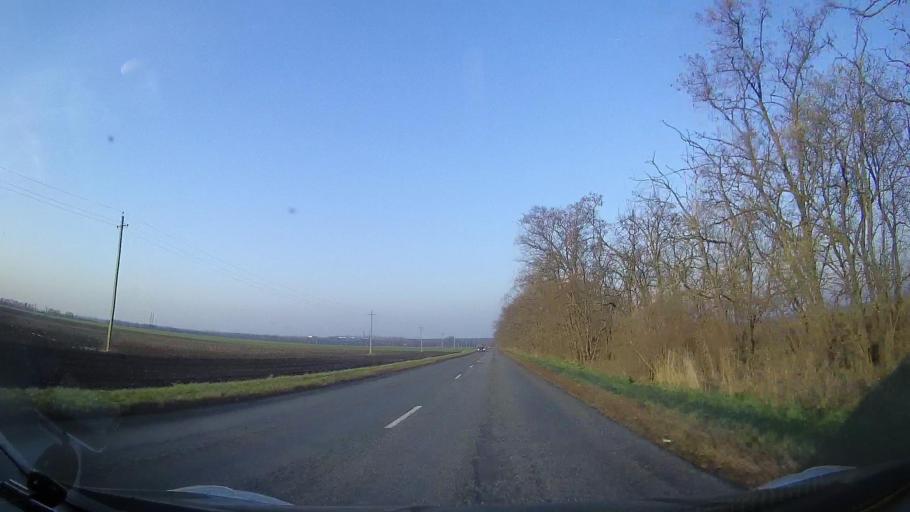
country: RU
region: Rostov
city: Ol'ginskaya
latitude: 47.1004
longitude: 39.9776
